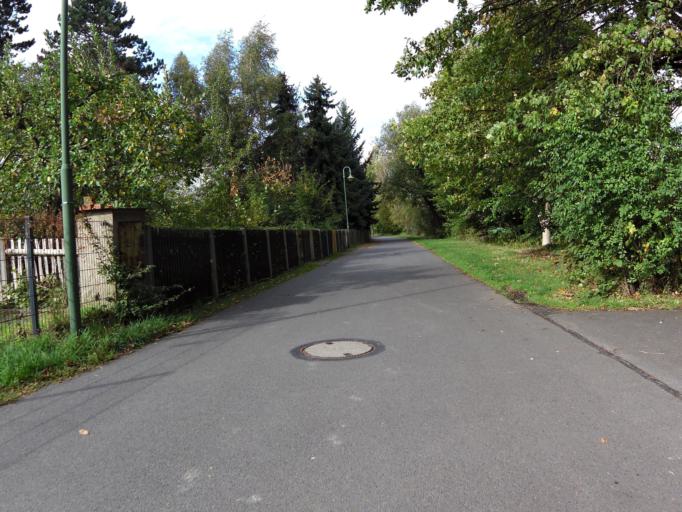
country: DE
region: Saxony
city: Grossposna
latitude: 51.2922
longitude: 12.4495
